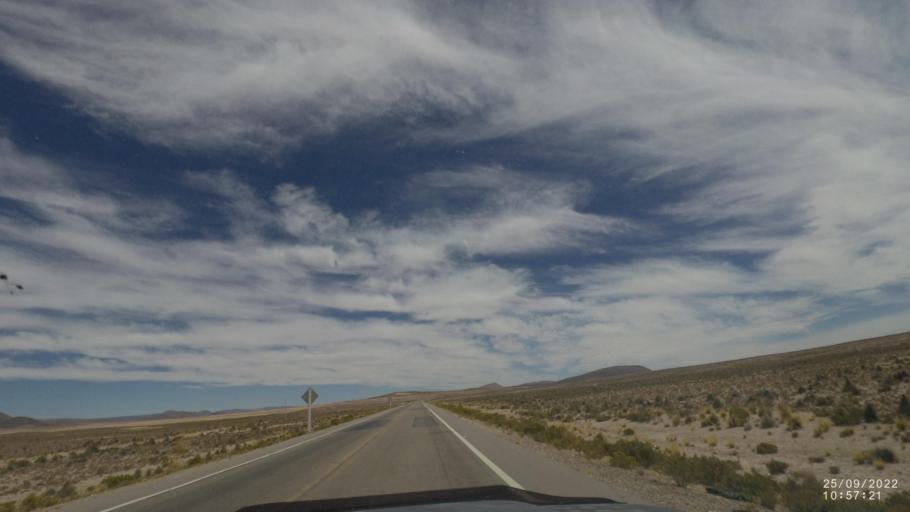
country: BO
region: Oruro
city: Challapata
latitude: -19.4756
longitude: -66.8898
